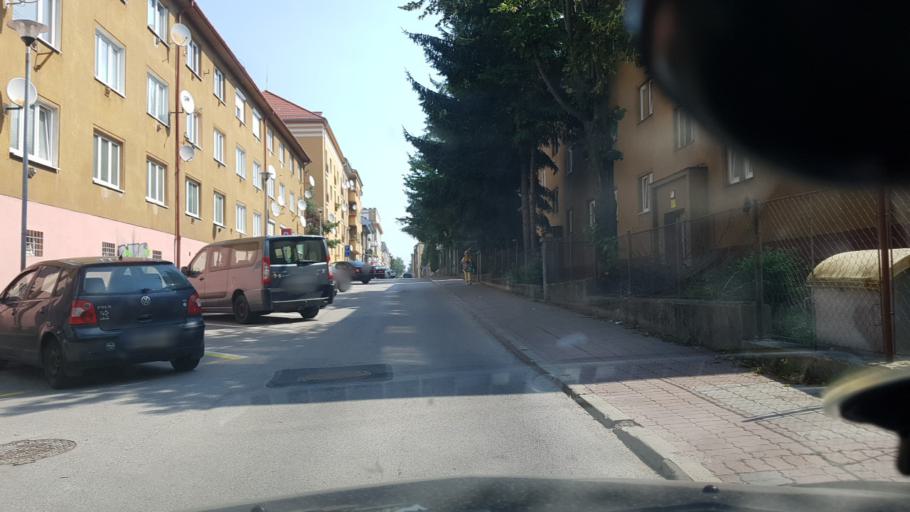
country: SK
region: Banskobystricky
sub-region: Okres Banska Bystrica
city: Banska Bystrica
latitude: 48.7325
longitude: 19.1427
